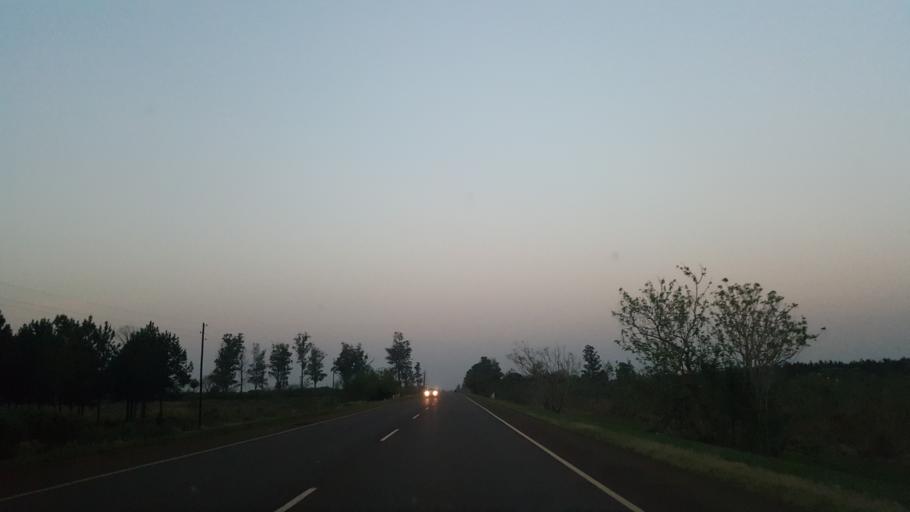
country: AR
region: Misiones
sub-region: Departamento de Capital
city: Posadas
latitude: -27.4247
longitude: -55.9984
